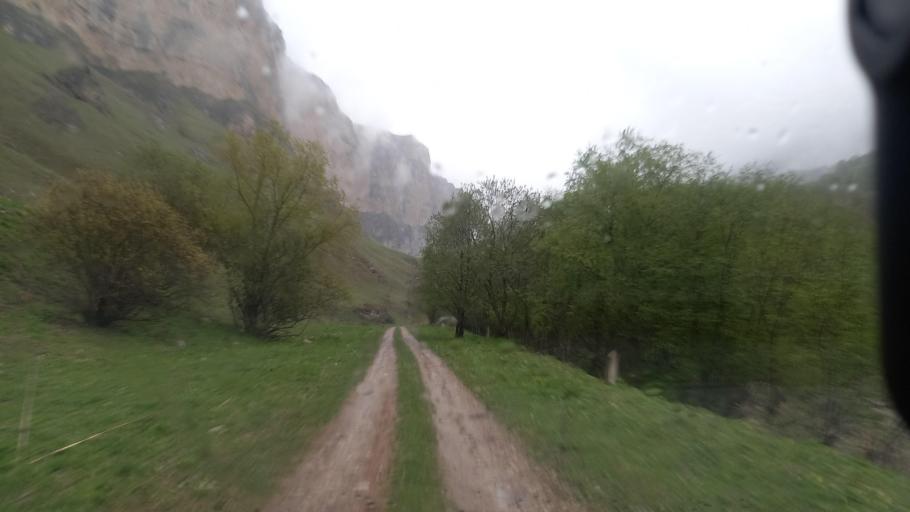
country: RU
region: Kabardino-Balkariya
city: Bylym
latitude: 43.5963
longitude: 42.9577
